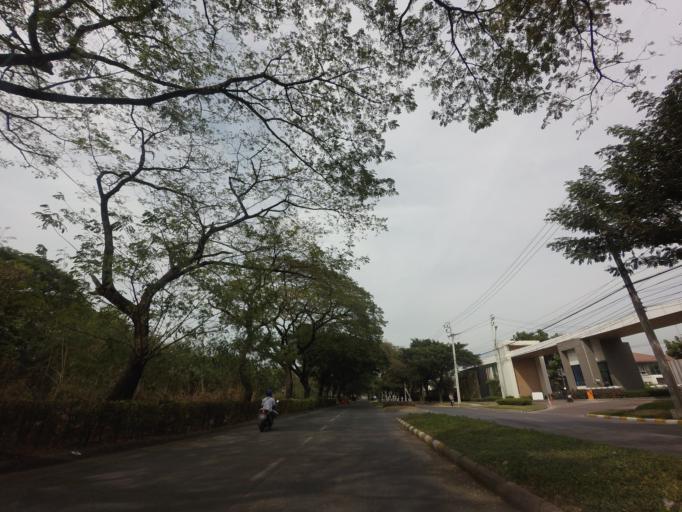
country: TH
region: Bangkok
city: Khlong Sam Wa
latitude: 13.8731
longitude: 100.7085
